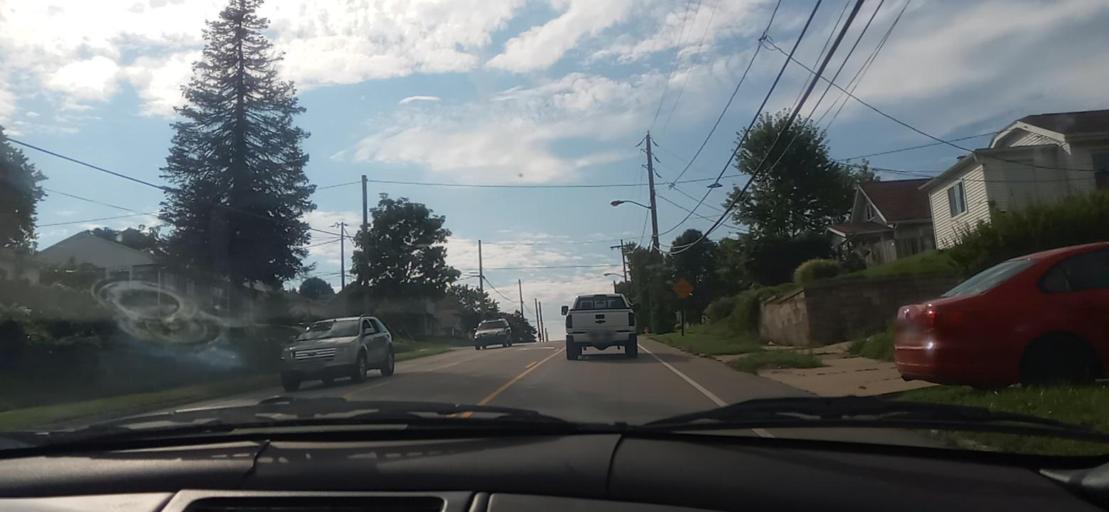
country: US
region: Ohio
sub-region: Summit County
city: Portage Lakes
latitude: 41.0293
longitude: -81.5405
